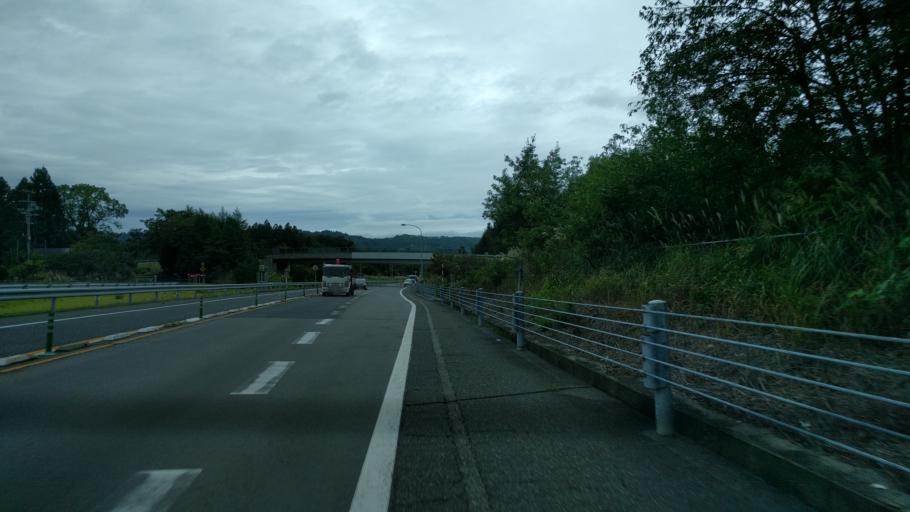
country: JP
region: Fukushima
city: Kitakata
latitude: 37.5615
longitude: 139.7689
